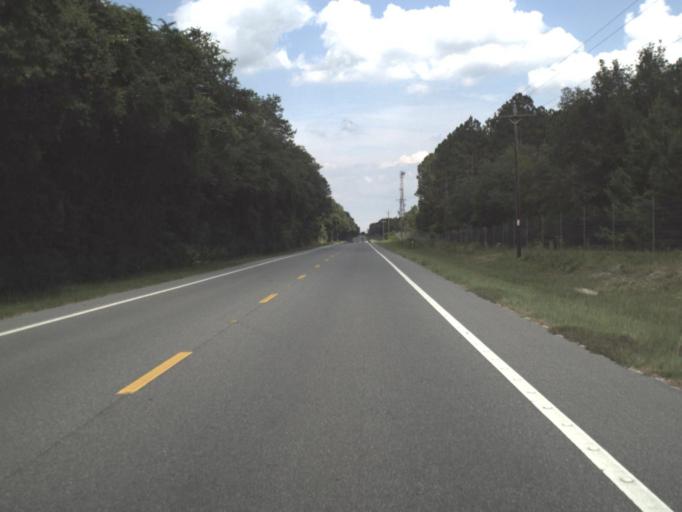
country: US
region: Florida
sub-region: Putnam County
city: Interlachen
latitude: 29.7248
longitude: -81.8371
